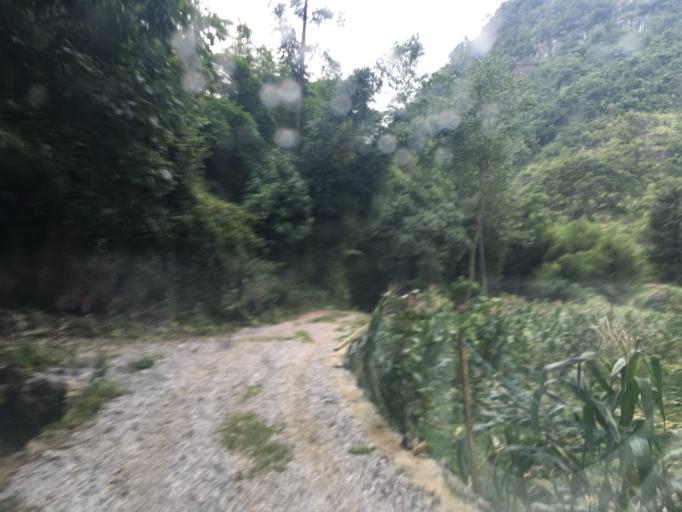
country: CN
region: Guangxi Zhuangzu Zizhiqu
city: Xinzhou
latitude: 25.2275
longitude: 105.6283
